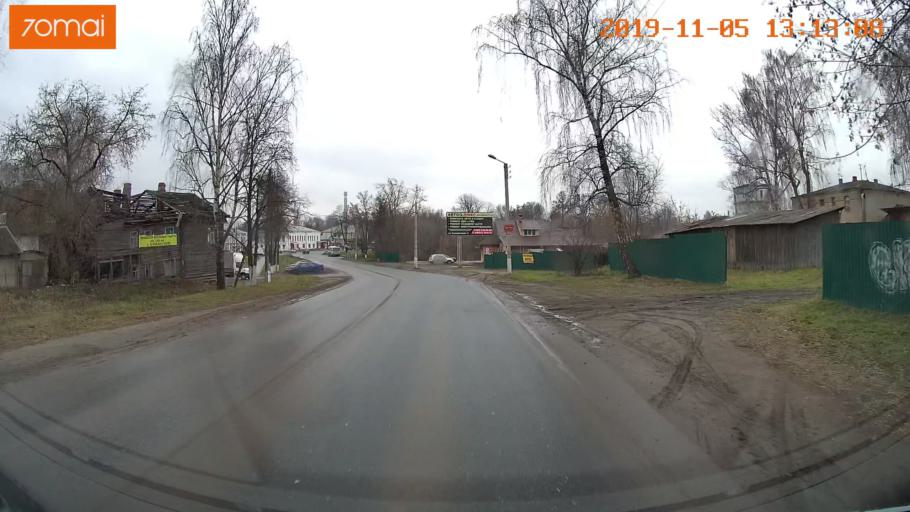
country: RU
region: Ivanovo
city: Shuya
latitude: 56.8529
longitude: 41.3532
